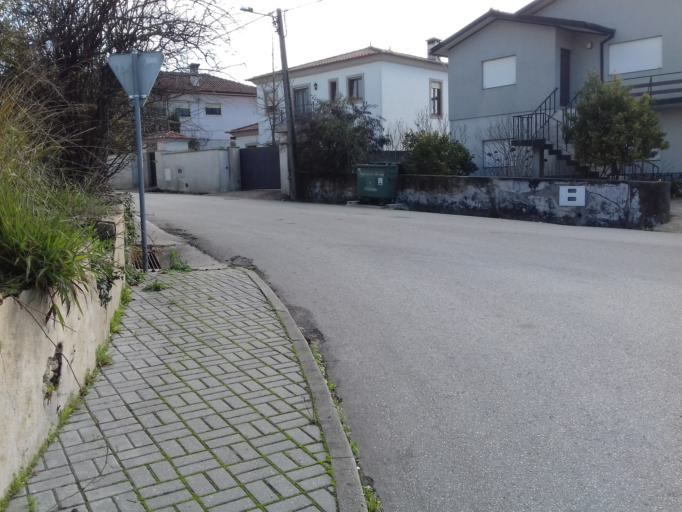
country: PT
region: Aveiro
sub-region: Albergaria-A-Velha
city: Branca
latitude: 40.7634
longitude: -8.4826
